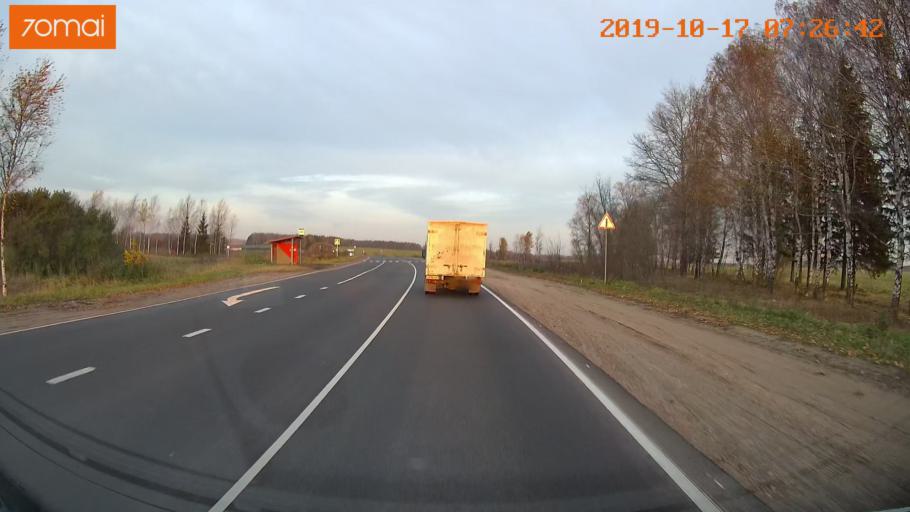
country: RU
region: Ivanovo
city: Gavrilov Posad
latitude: 56.3594
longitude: 40.0902
